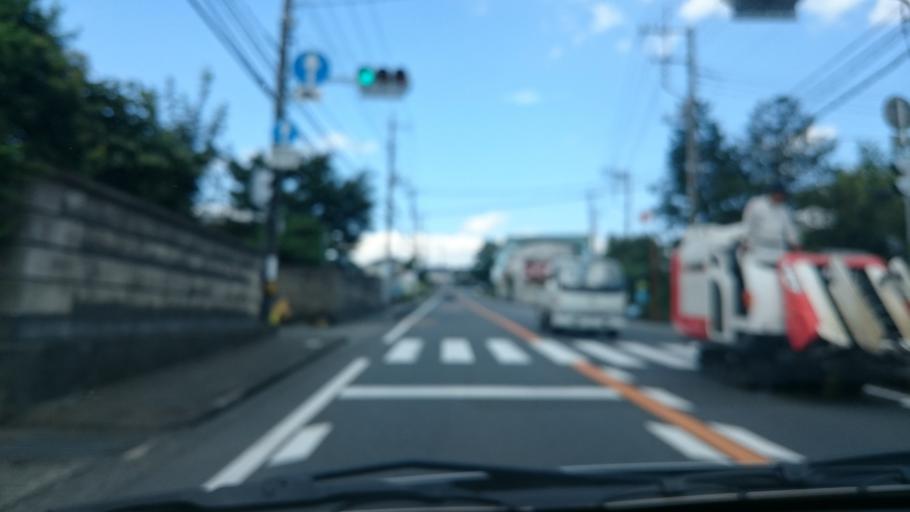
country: JP
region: Shizuoka
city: Gotemba
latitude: 35.2319
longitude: 138.9207
